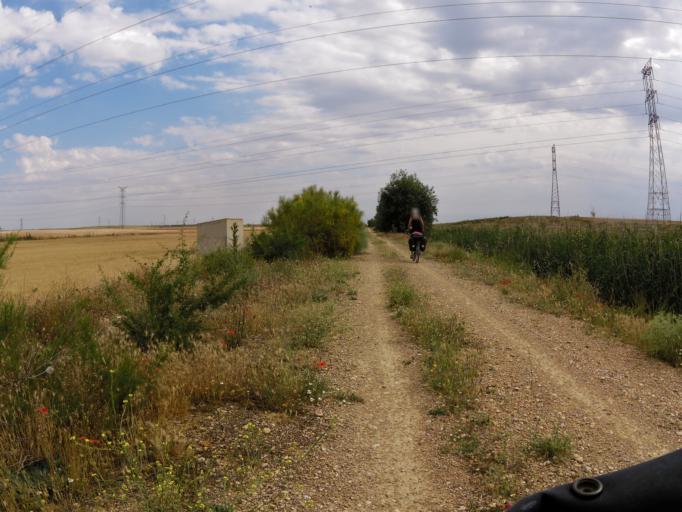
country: ES
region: Castille-La Mancha
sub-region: Provincia de Albacete
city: Albacete
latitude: 39.0342
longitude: -1.7897
